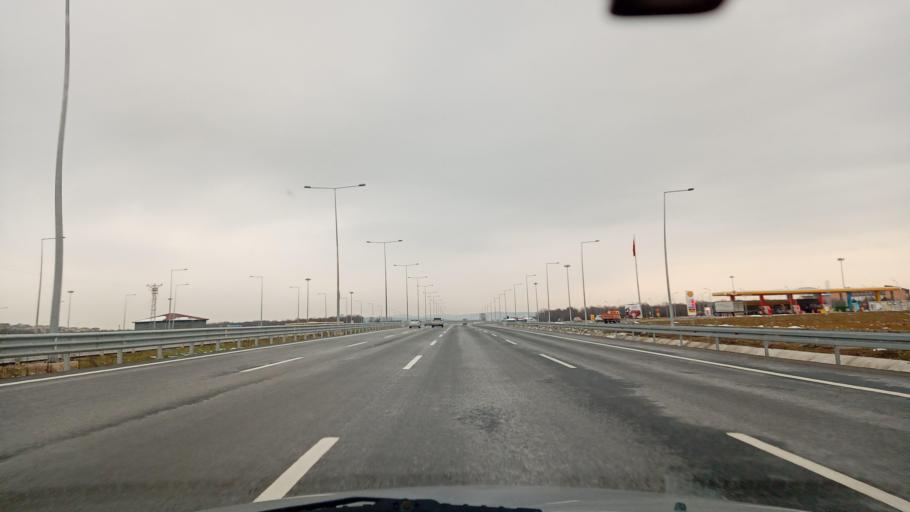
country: TR
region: Sakarya
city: Kazimpasa
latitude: 40.8440
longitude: 30.2815
